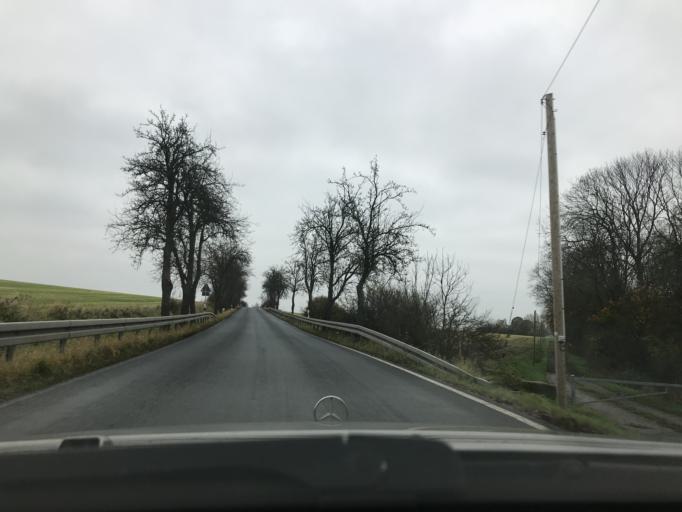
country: DE
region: Thuringia
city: Muehlhausen
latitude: 51.2560
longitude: 10.4145
